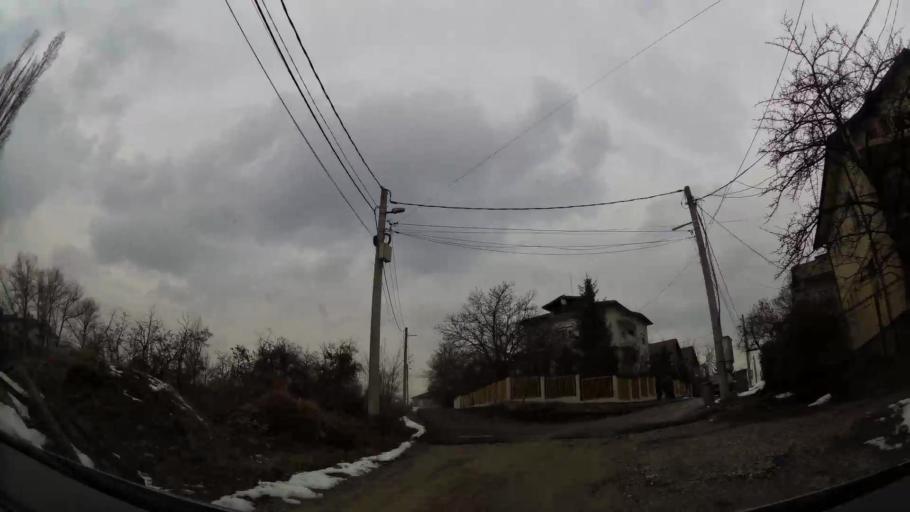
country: BG
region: Sofiya
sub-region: Obshtina Bozhurishte
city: Bozhurishte
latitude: 42.6716
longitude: 23.2388
